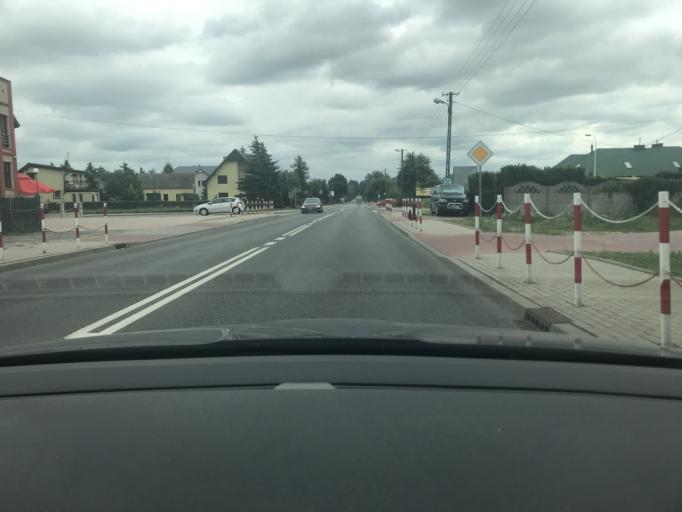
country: PL
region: Lodz Voivodeship
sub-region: Powiat poddebicki
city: Poddebice
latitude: 51.8928
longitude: 18.9630
